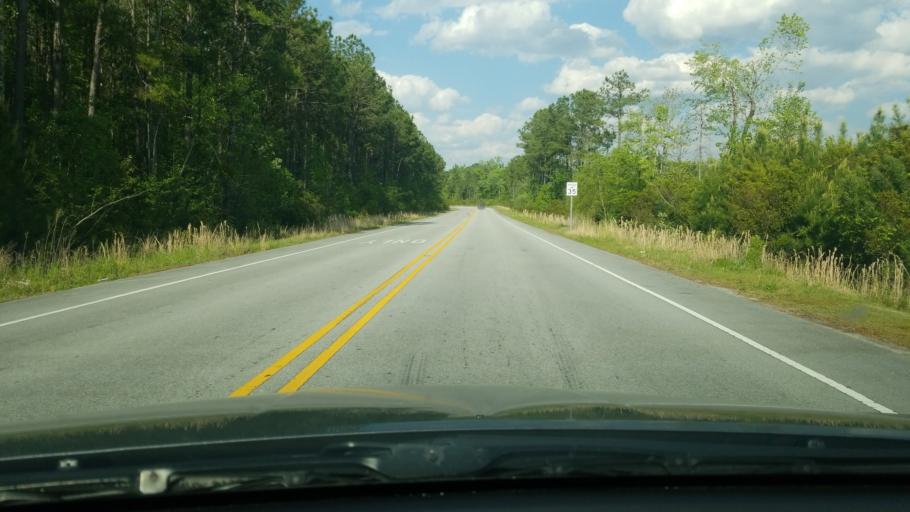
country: US
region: North Carolina
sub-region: Onslow County
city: Pumpkin Center
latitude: 34.7767
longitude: -77.4004
